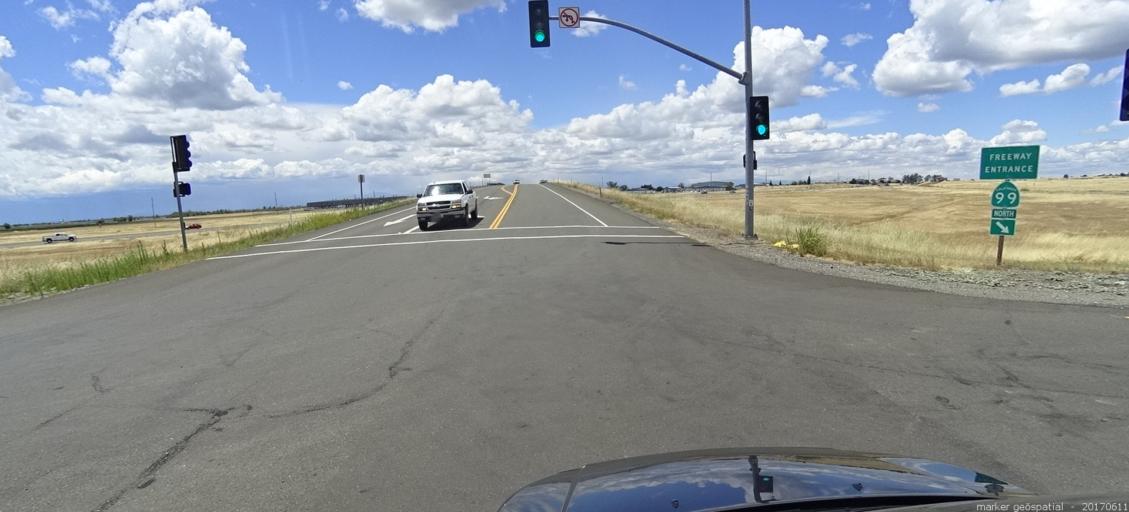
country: US
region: California
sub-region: Butte County
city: Durham
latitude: 39.6423
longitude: -121.7136
